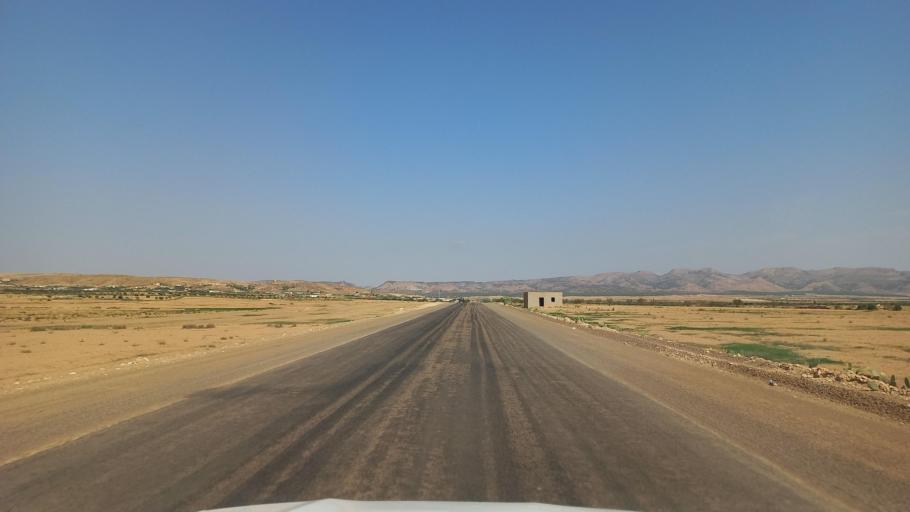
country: TN
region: Al Qasrayn
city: Sbiba
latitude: 35.3714
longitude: 9.0364
